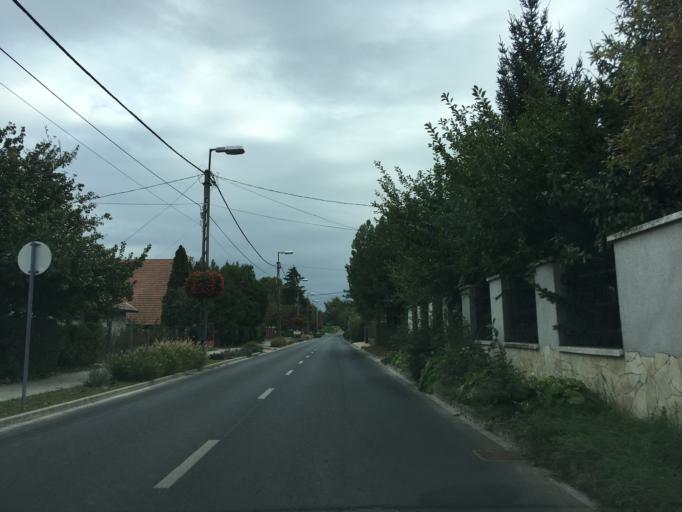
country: HU
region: Pest
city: Szazhalombatta
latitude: 47.3118
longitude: 18.9241
